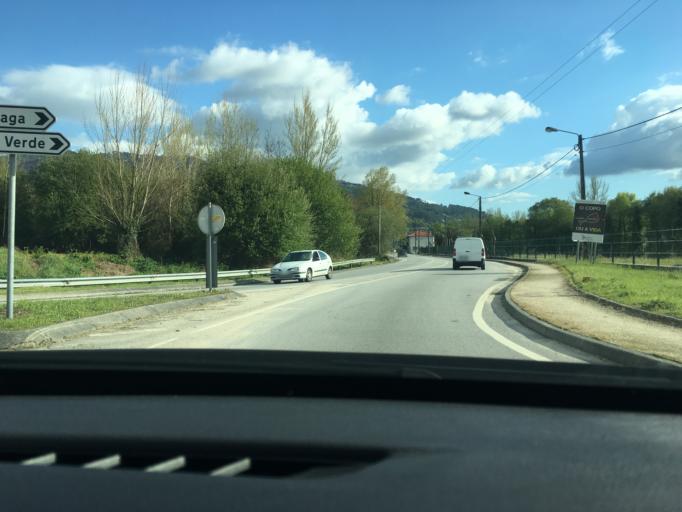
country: PT
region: Viana do Castelo
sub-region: Ponte da Barca
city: Ponte da Barca
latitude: 41.7917
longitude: -8.4140
